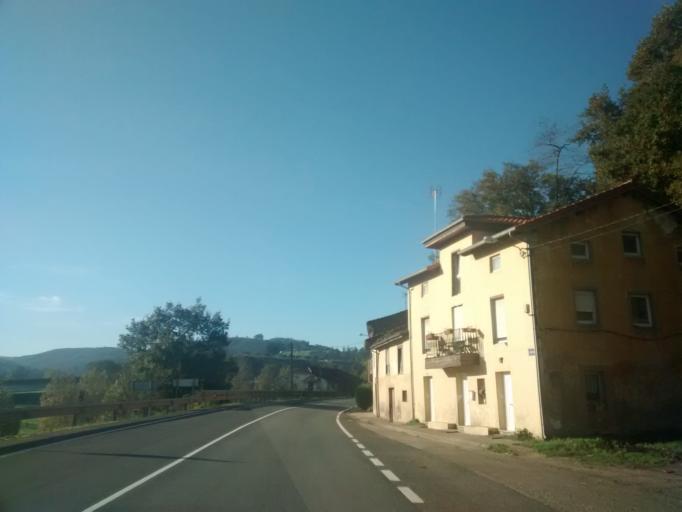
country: ES
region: Cantabria
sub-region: Provincia de Cantabria
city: Penagos
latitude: 43.3455
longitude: -3.7906
